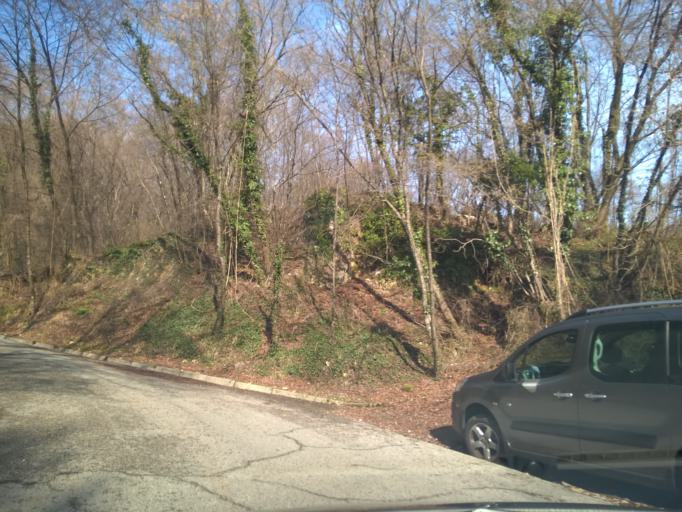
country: IT
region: Veneto
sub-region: Provincia di Vicenza
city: Piovene Rocchette
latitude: 45.7610
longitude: 11.4249
